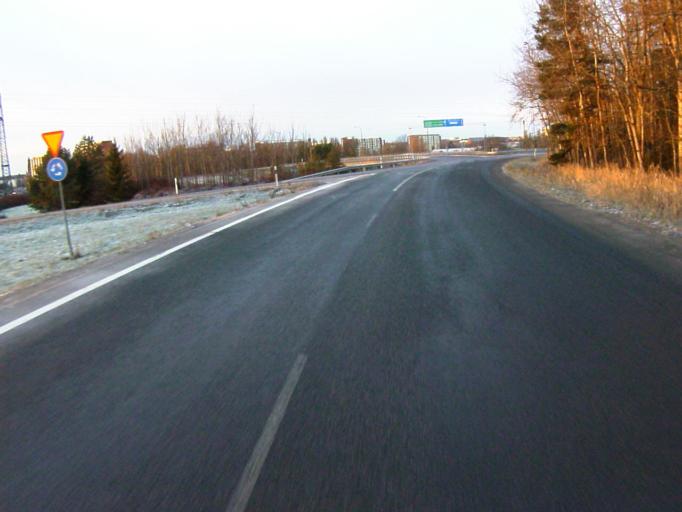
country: SE
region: Soedermanland
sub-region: Eskilstuna Kommun
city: Eskilstuna
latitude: 59.3873
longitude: 16.5271
